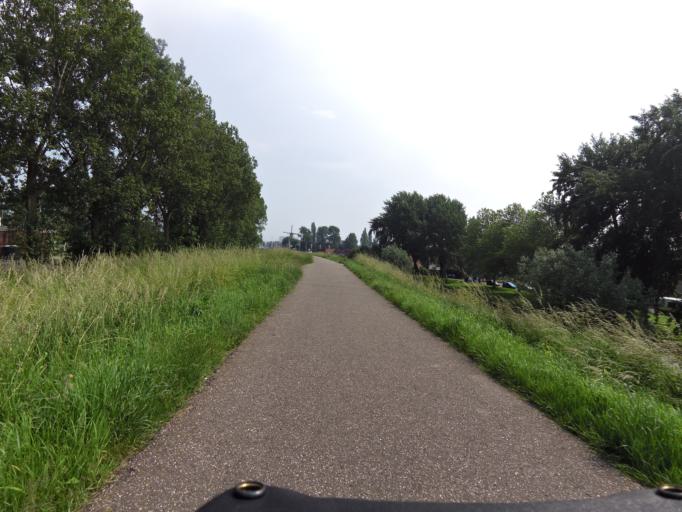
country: NL
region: South Holland
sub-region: Gemeente Spijkenisse
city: Spijkenisse
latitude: 51.8568
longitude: 4.3274
